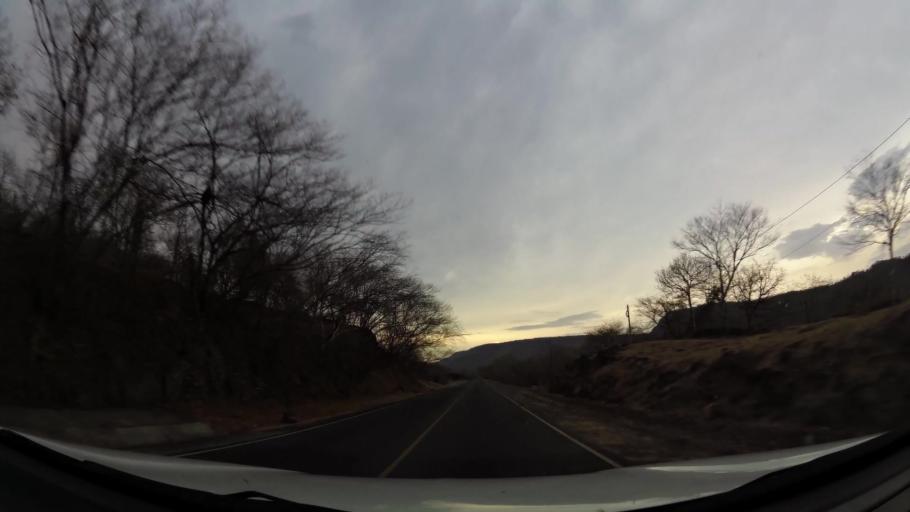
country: NI
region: Leon
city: La Jicaral
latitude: 12.6826
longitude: -86.4232
